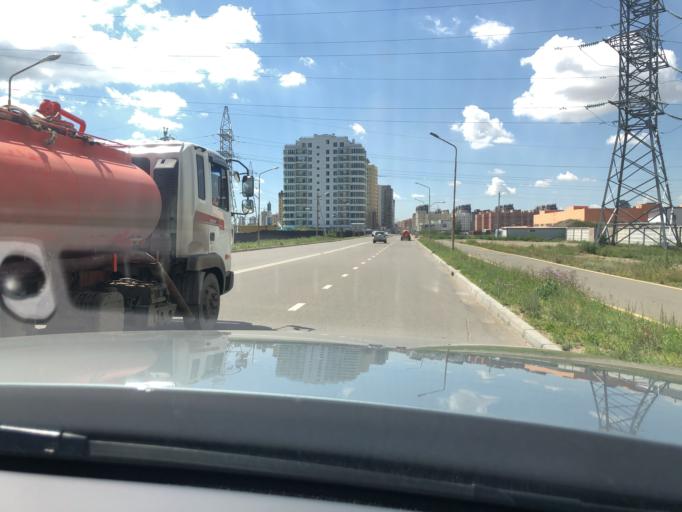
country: MN
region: Ulaanbaatar
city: Ulaanbaatar
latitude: 47.9048
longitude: 106.9551
